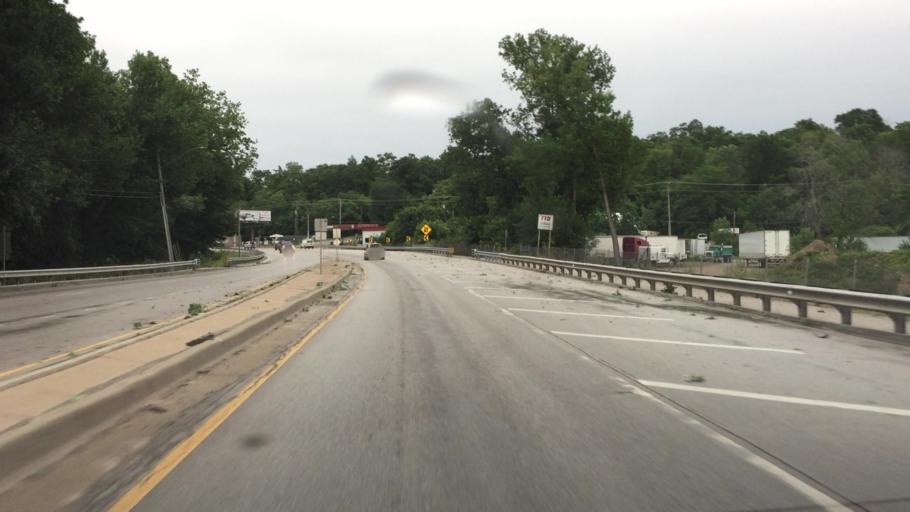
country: US
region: Illinois
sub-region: Hancock County
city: Hamilton
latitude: 40.3904
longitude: -91.3583
